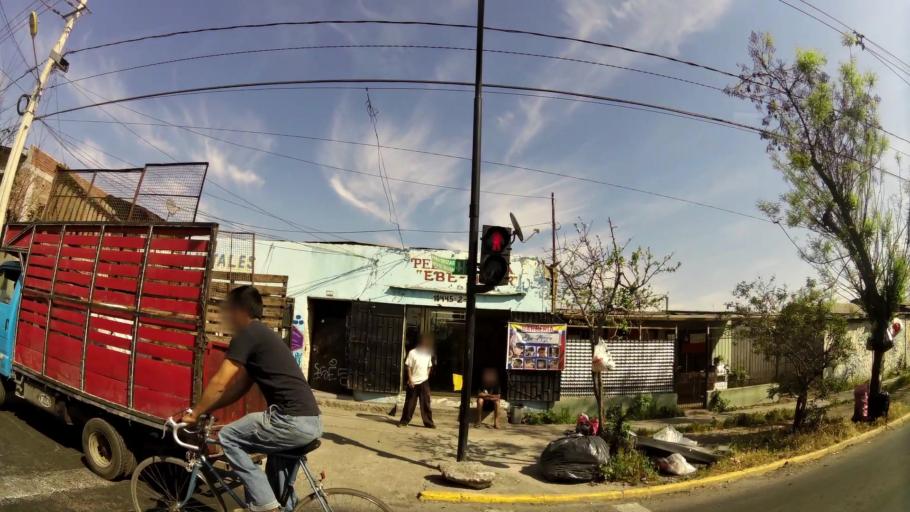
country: CL
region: Santiago Metropolitan
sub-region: Provincia de Santiago
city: La Pintana
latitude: -33.5596
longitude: -70.6562
